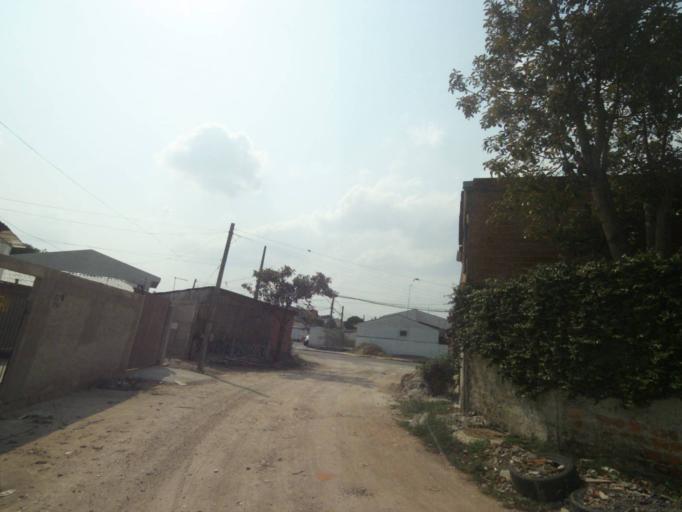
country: BR
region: Parana
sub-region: Sao Jose Dos Pinhais
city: Sao Jose dos Pinhais
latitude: -25.5289
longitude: -49.2347
